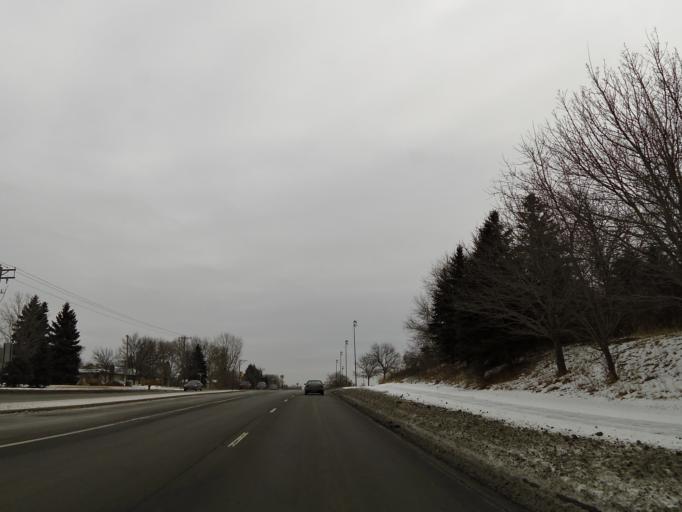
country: US
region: Minnesota
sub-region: Scott County
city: Savage
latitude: 44.8079
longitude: -93.3913
